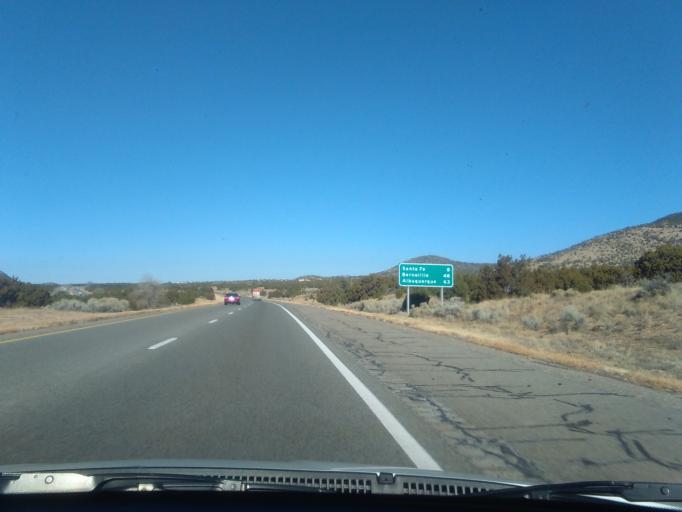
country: US
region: New Mexico
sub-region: Santa Fe County
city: Eldorado at Santa Fe
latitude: 35.5658
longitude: -105.8853
